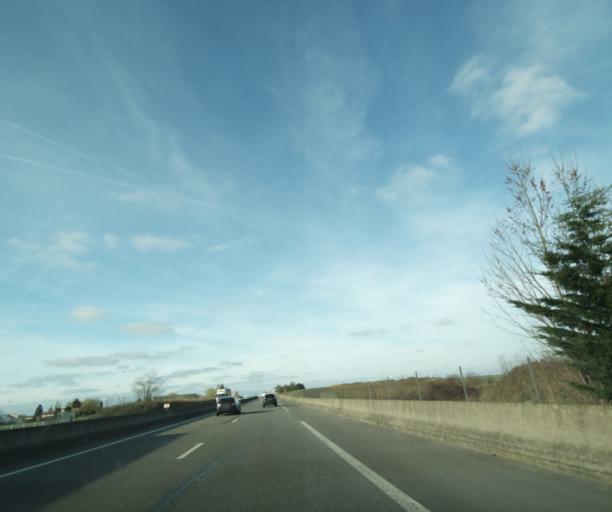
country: FR
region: Ile-de-France
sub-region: Departement des Yvelines
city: Ablis
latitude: 48.5630
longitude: 1.8324
